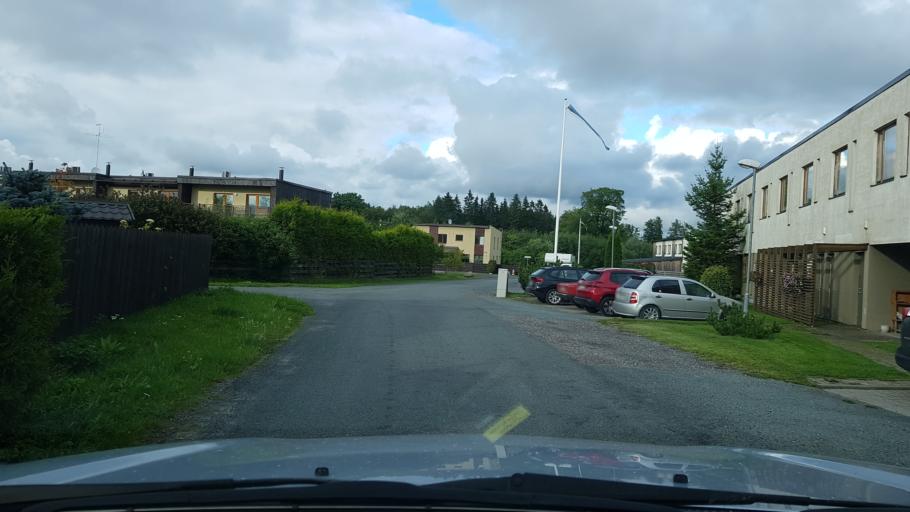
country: EE
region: Harju
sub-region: Rae vald
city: Jueri
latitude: 59.3635
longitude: 24.9195
